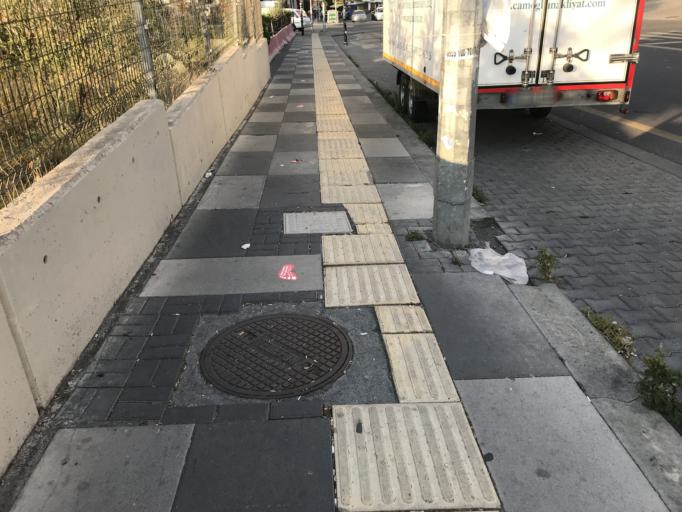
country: TR
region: Ankara
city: Ankara
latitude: 39.8724
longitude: 32.8319
